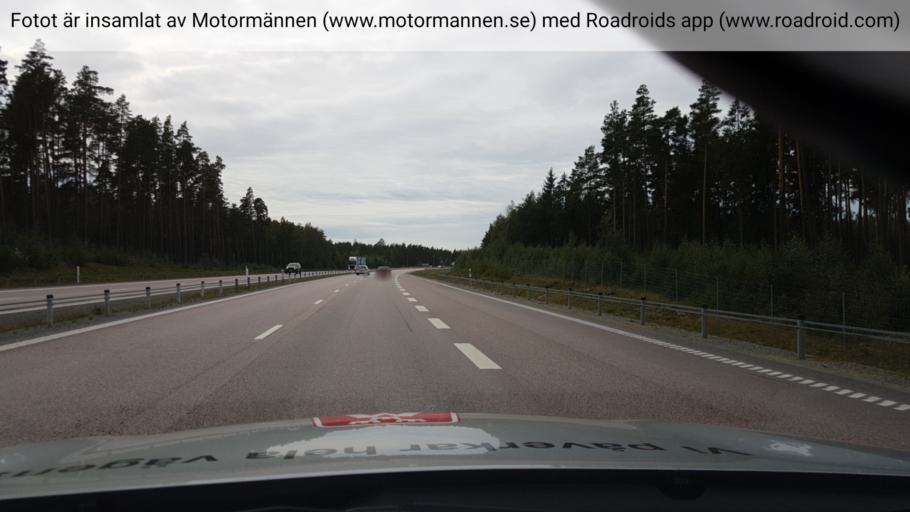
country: SE
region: Uppsala
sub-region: Enkopings Kommun
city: Hummelsta
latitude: 59.6252
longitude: 16.8308
